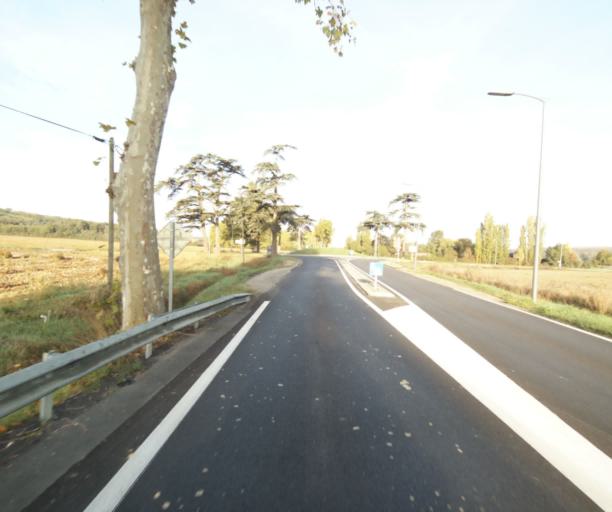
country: FR
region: Midi-Pyrenees
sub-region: Departement du Tarn-et-Garonne
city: Saint-Nauphary
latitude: 43.9438
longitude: 1.4644
